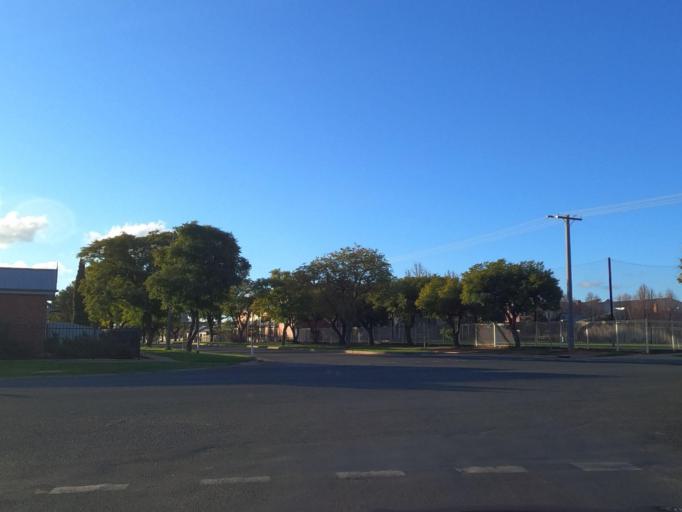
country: AU
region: Victoria
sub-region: Swan Hill
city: Swan Hill
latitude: -35.3438
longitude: 143.5563
